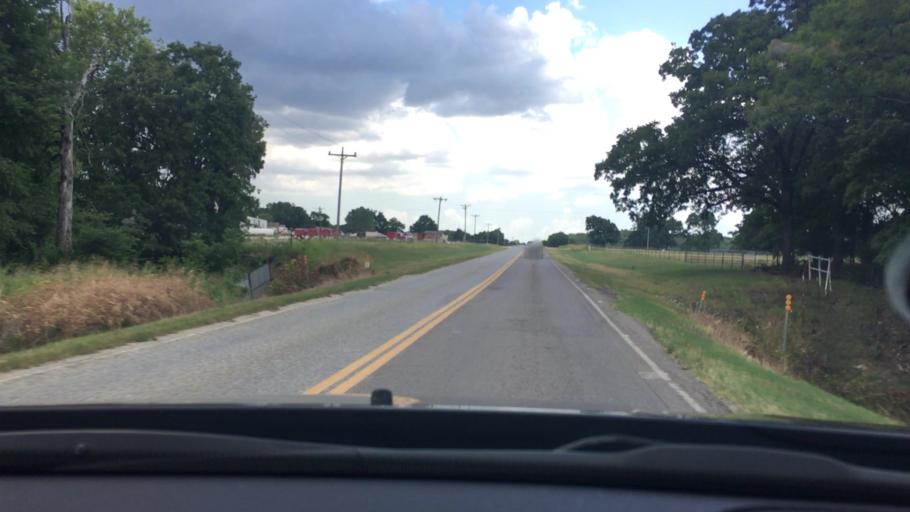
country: US
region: Oklahoma
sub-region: Pontotoc County
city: Ada
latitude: 34.5906
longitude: -96.6347
